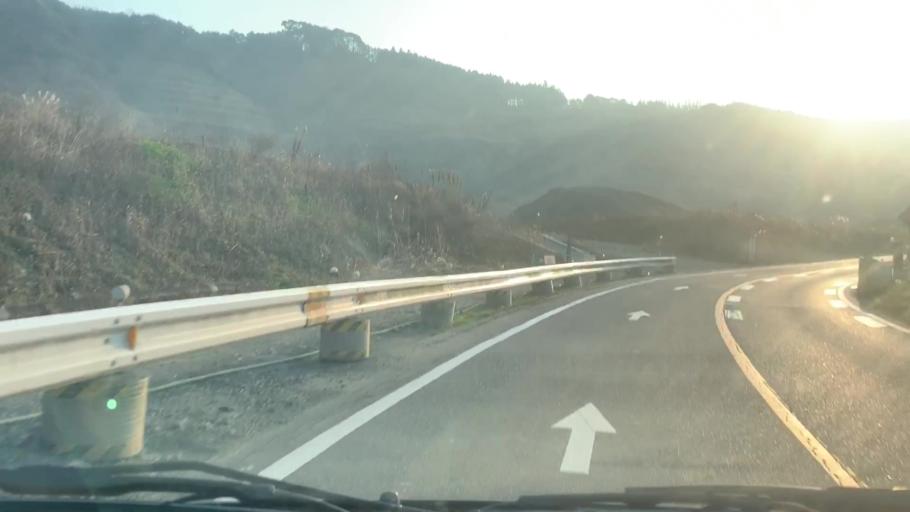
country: JP
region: Saga Prefecture
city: Takeocho-takeo
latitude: 33.2710
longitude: 130.1120
